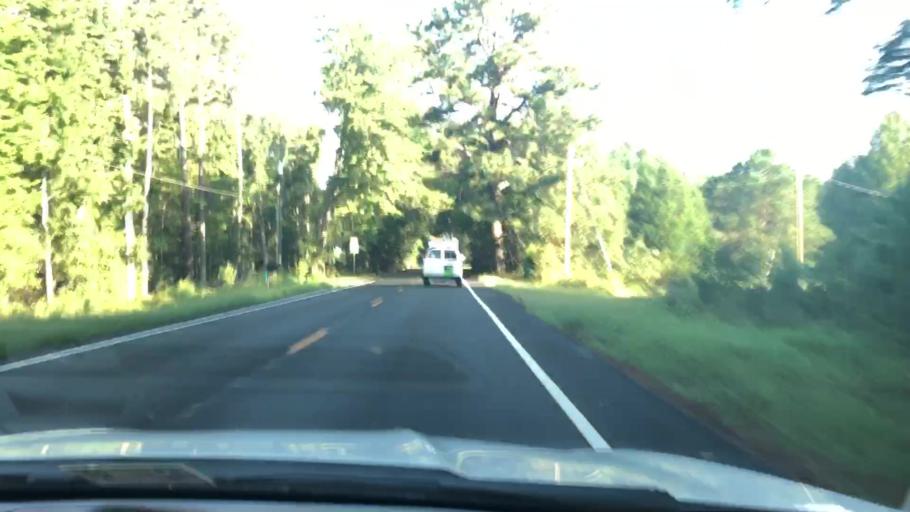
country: US
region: Virginia
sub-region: King William County
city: West Point
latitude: 37.4677
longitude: -76.8438
